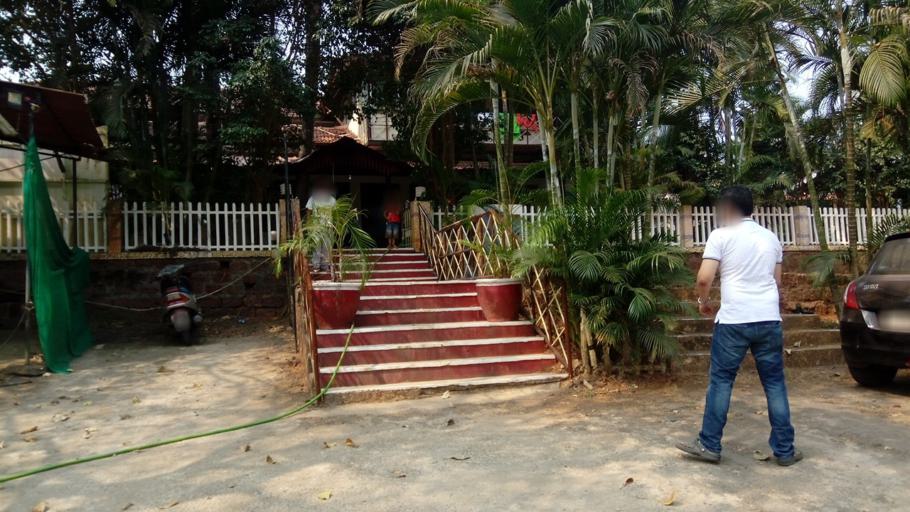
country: IN
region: Goa
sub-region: South Goa
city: Varca
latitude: 15.2188
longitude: 73.9338
